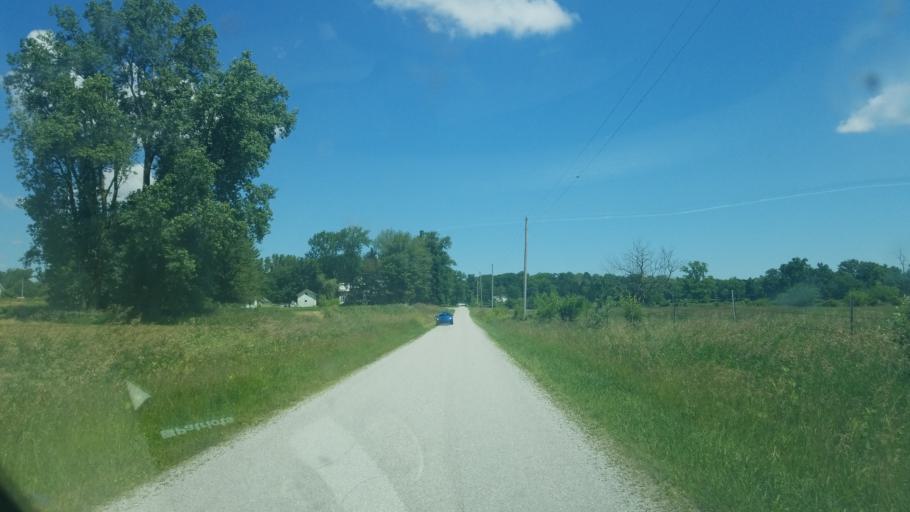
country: US
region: Ohio
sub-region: Huron County
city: New London
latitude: 41.1514
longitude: -82.3895
